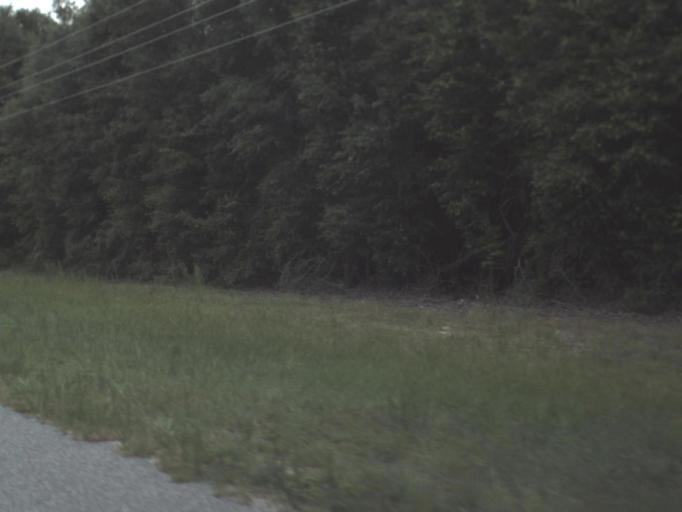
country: US
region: Florida
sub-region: Hamilton County
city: Jasper
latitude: 30.5078
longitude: -83.0667
